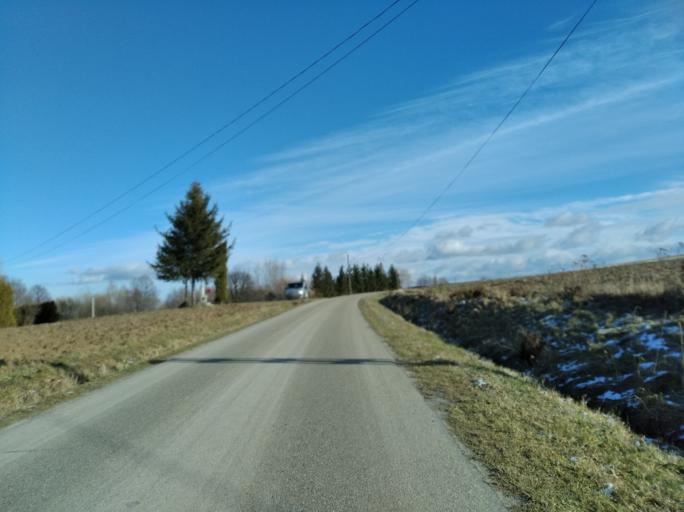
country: PL
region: Subcarpathian Voivodeship
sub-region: Powiat ropczycko-sedziszowski
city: Wielopole Skrzynskie
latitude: 49.9170
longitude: 21.6310
